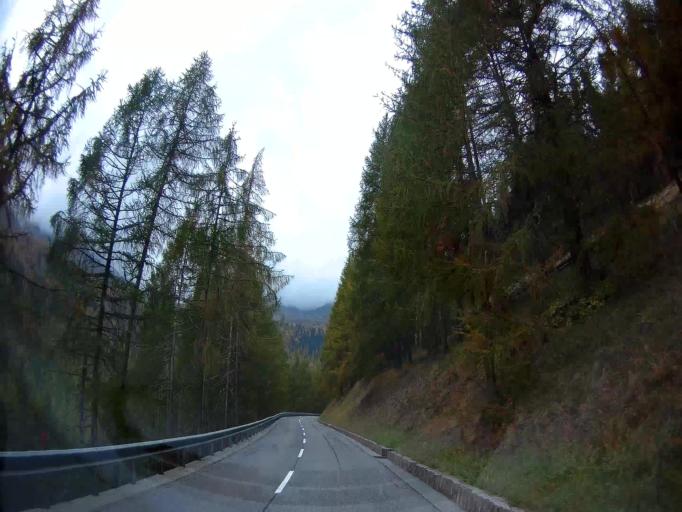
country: IT
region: Trentino-Alto Adige
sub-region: Bolzano
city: Senales
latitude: 46.7360
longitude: 10.8209
